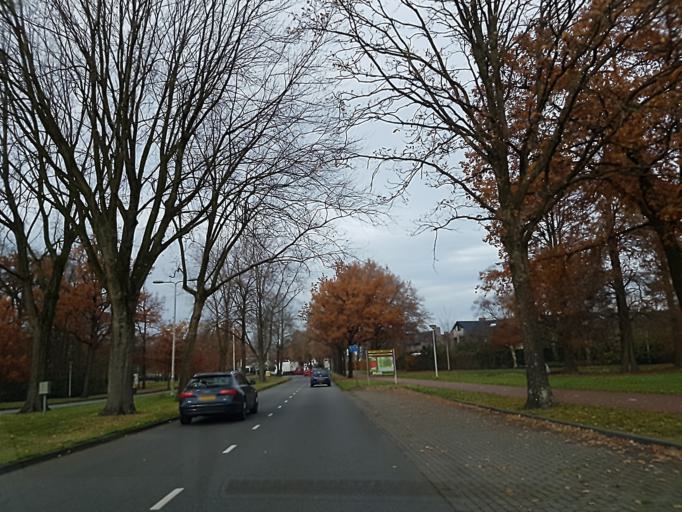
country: NL
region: North Brabant
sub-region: Roosendaal
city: Roosendaal
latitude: 51.5275
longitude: 4.4654
